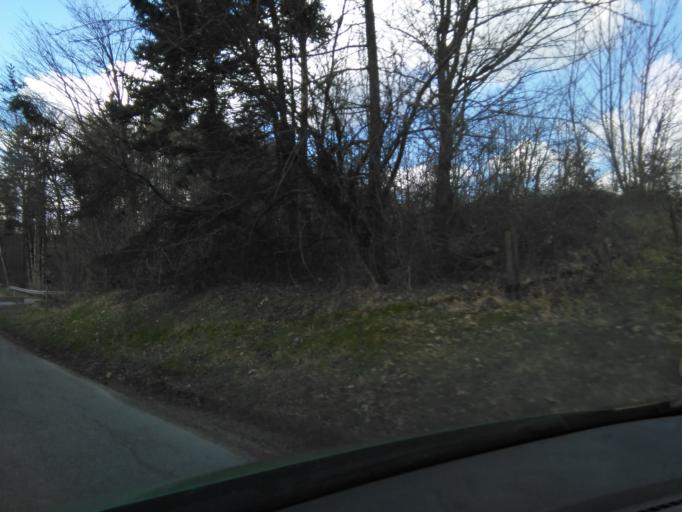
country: DK
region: Central Jutland
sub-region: Silkeborg Kommune
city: Virklund
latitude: 56.0413
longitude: 9.4477
